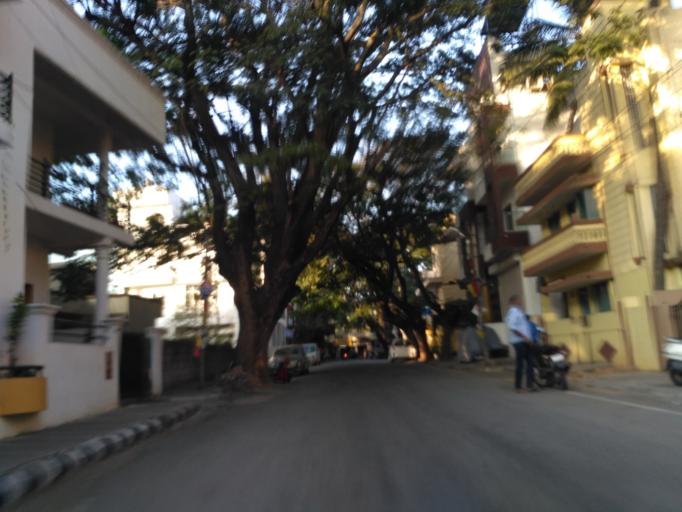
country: IN
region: Karnataka
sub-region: Bangalore Urban
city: Bangalore
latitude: 12.9674
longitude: 77.5386
